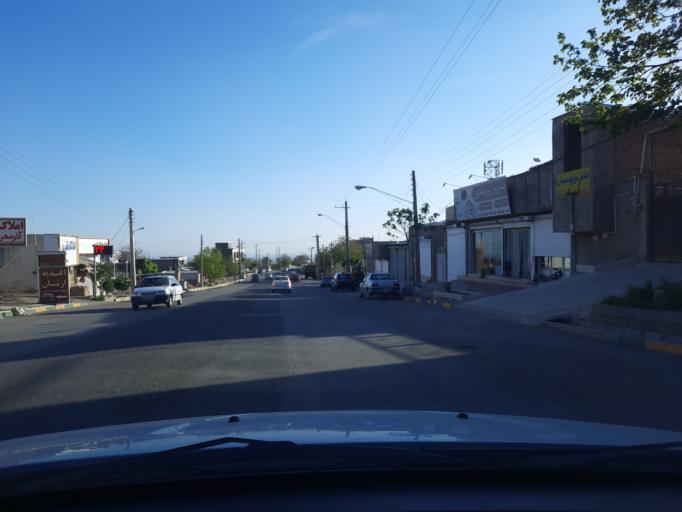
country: IR
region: Qazvin
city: Qazvin
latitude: 36.3324
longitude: 50.1511
